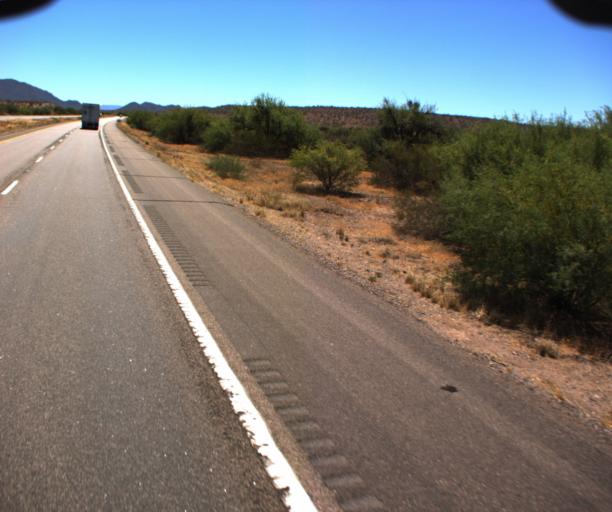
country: US
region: Arizona
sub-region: Maricopa County
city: Fountain Hills
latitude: 33.5822
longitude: -111.6545
